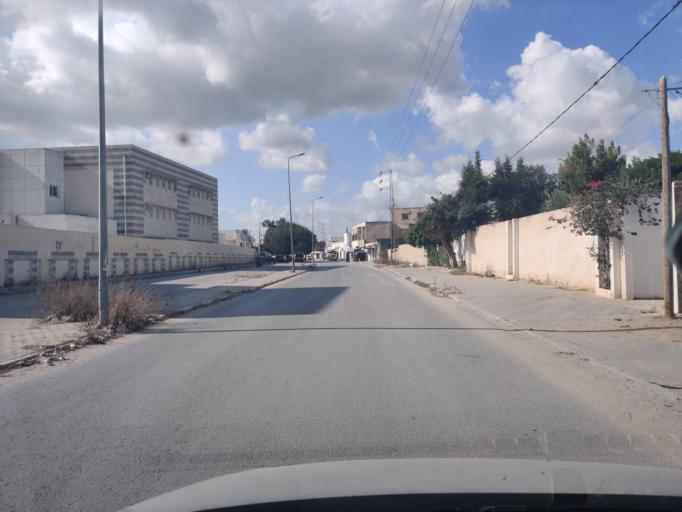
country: TN
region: Tunis
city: Al Marsa
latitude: 36.8817
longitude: 10.2742
